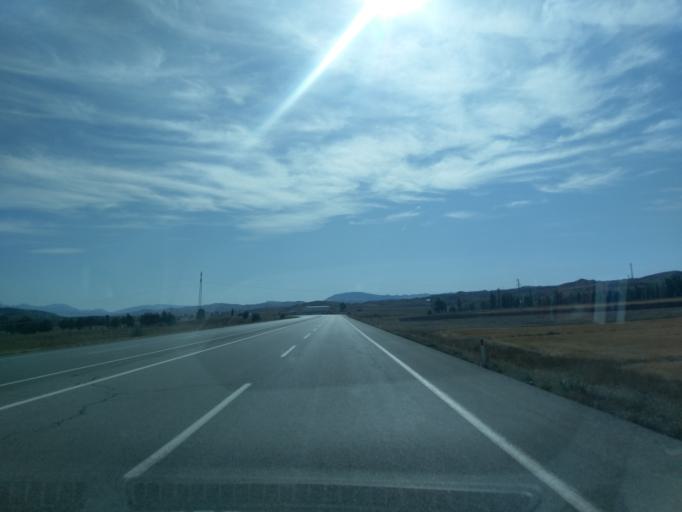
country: TR
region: Sivas
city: Imranli
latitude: 39.8767
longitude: 38.0761
